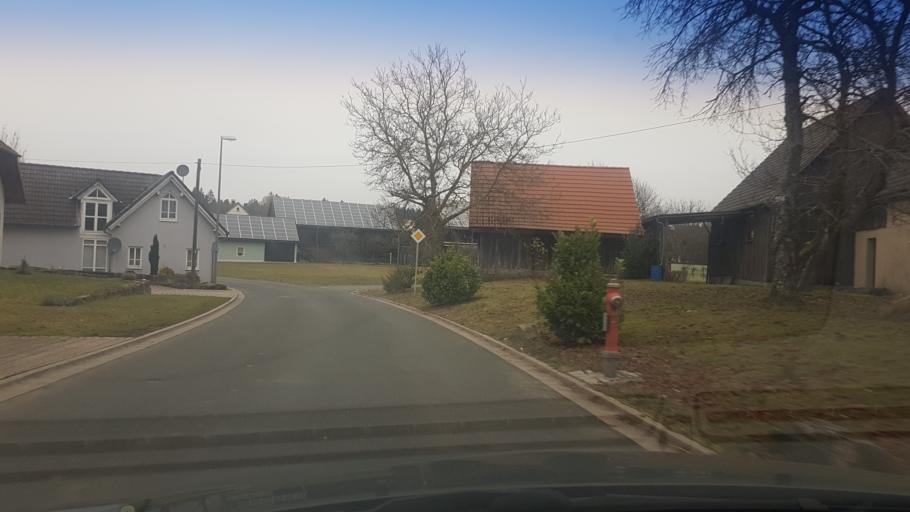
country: DE
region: Bavaria
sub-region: Upper Franconia
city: Stadelhofen
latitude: 50.0169
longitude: 11.2446
